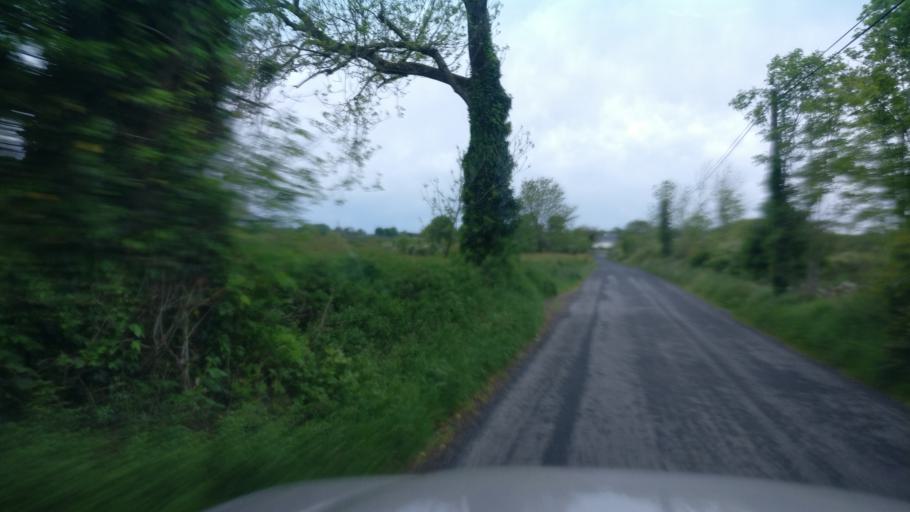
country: IE
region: Connaught
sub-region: County Galway
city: Loughrea
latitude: 53.1721
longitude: -8.4498
